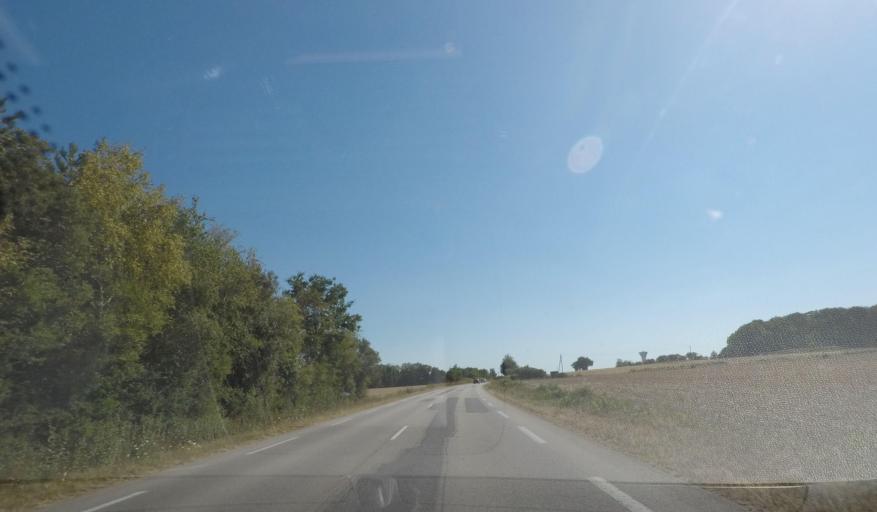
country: FR
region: Brittany
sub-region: Departement du Morbihan
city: Peaule
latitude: 47.5504
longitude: -2.3965
